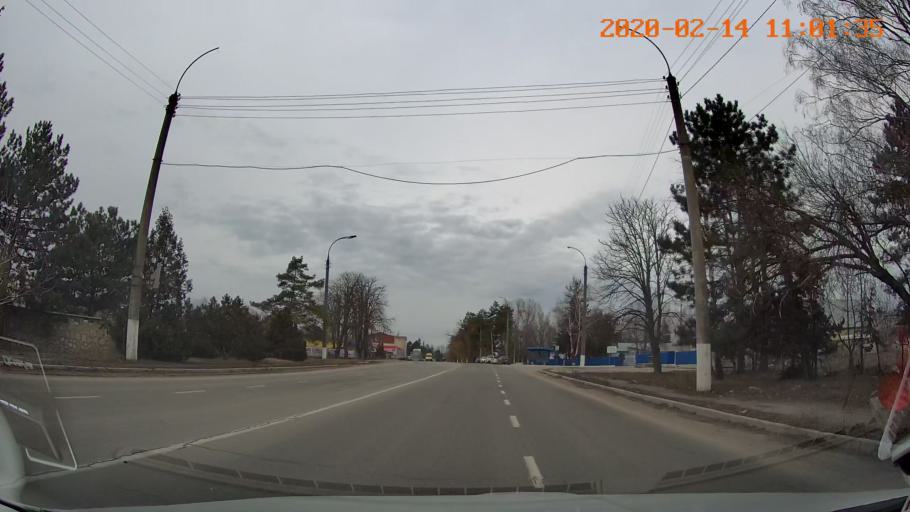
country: MD
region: Raionul Edinet
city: Edinet
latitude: 48.1606
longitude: 27.3279
